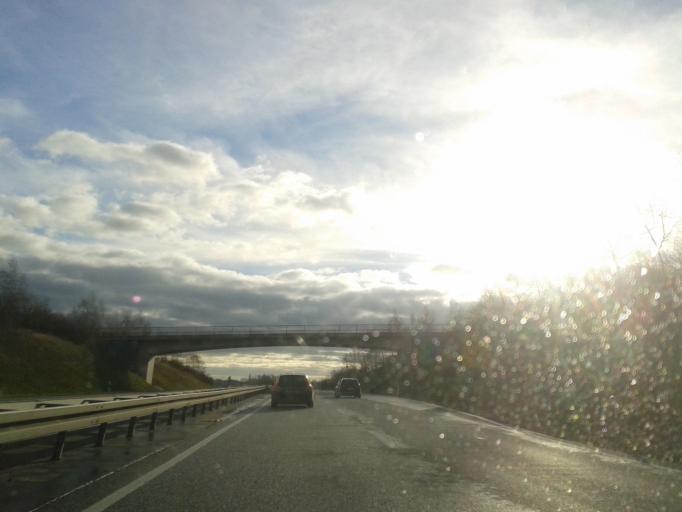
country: DE
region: Saxony
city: Grossschweidnitz
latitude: 51.0922
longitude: 14.6407
